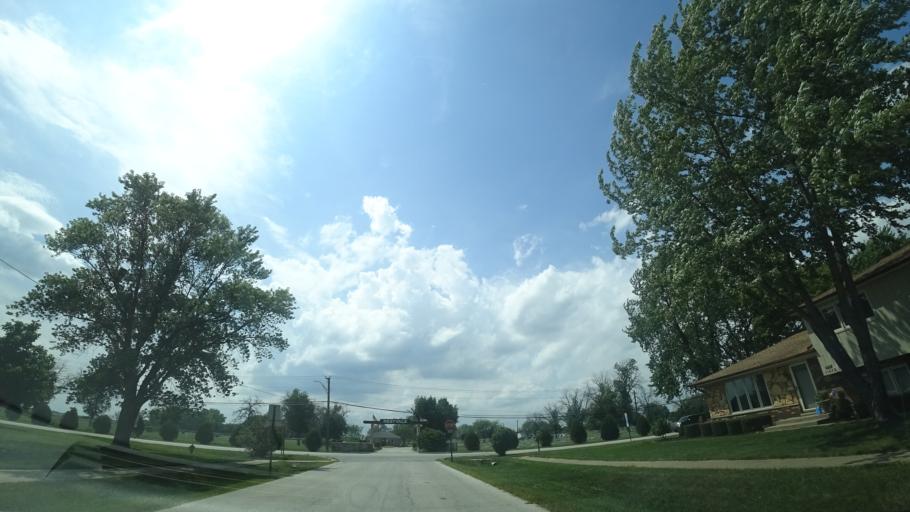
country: US
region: Illinois
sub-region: Cook County
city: Alsip
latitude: 41.6798
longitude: -87.7486
